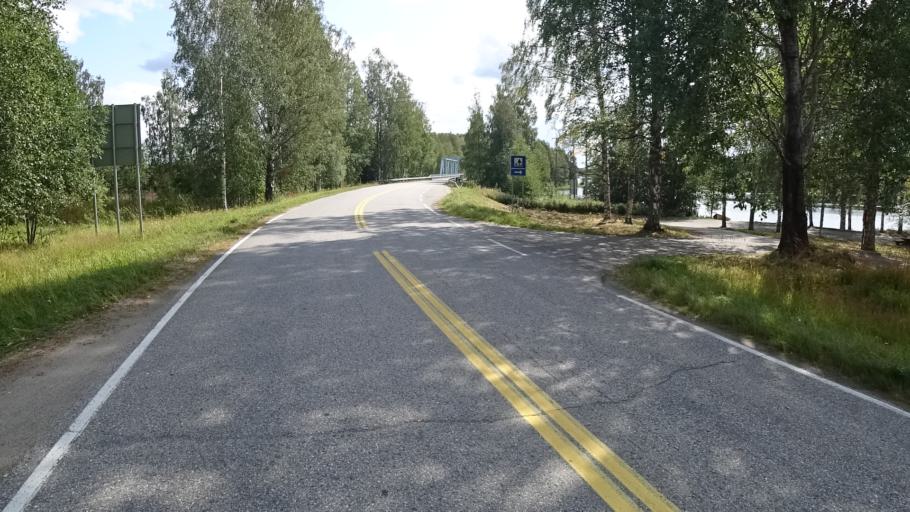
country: FI
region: North Karelia
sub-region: Joensuu
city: Ilomantsi
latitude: 62.6227
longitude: 31.1965
